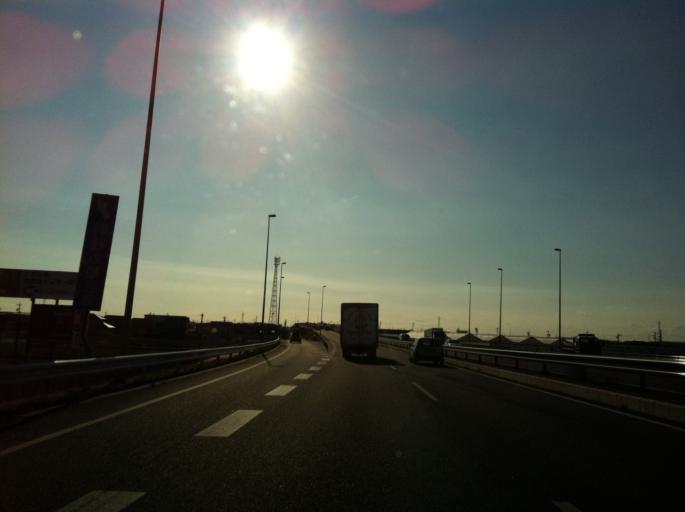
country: JP
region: Aichi
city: Toyohashi
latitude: 34.7457
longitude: 137.3374
